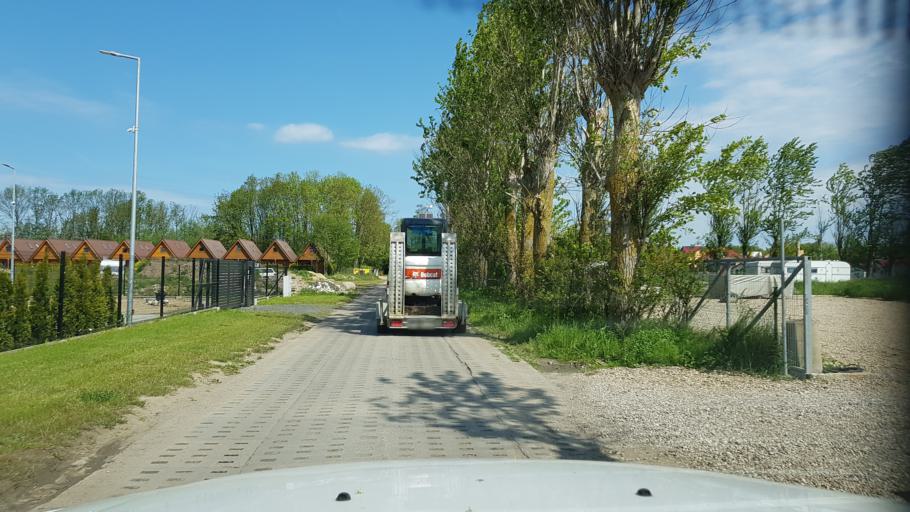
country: PL
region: West Pomeranian Voivodeship
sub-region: Powiat koszalinski
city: Mielno
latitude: 54.2436
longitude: 15.9560
